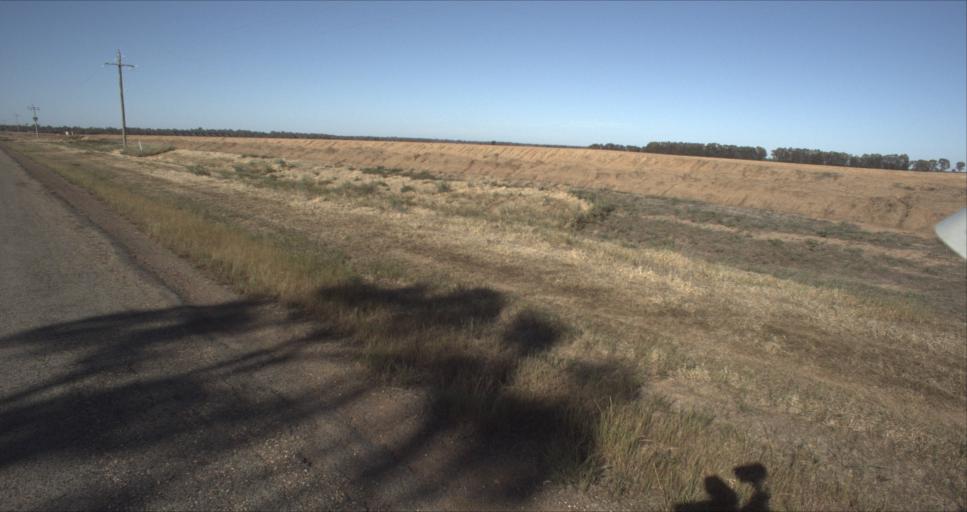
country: AU
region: New South Wales
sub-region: Leeton
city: Leeton
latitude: -34.5900
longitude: 146.2598
